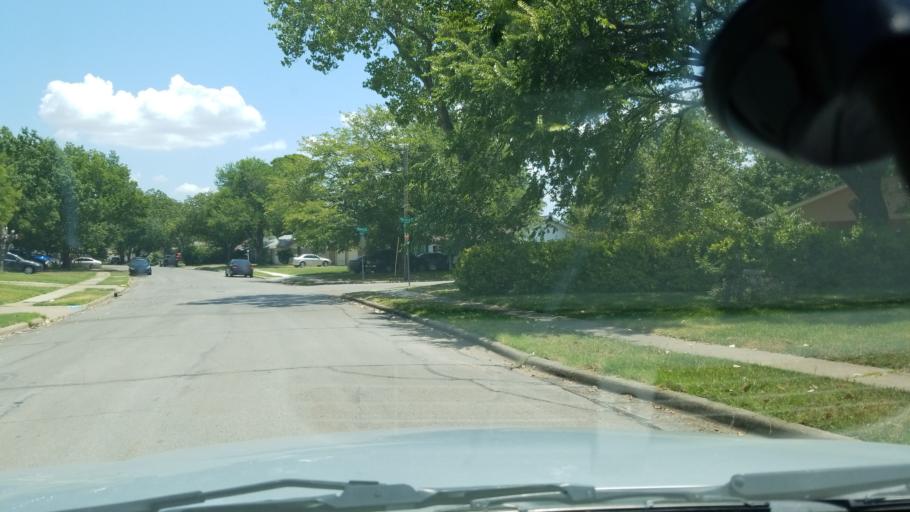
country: US
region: Texas
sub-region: Dallas County
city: Irving
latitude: 32.8233
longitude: -96.9899
